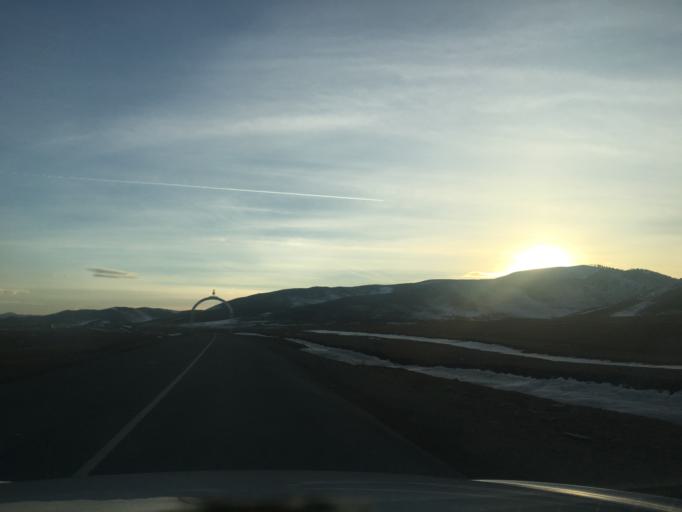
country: MN
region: Central Aimak
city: Mandal
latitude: 48.2332
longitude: 106.7214
